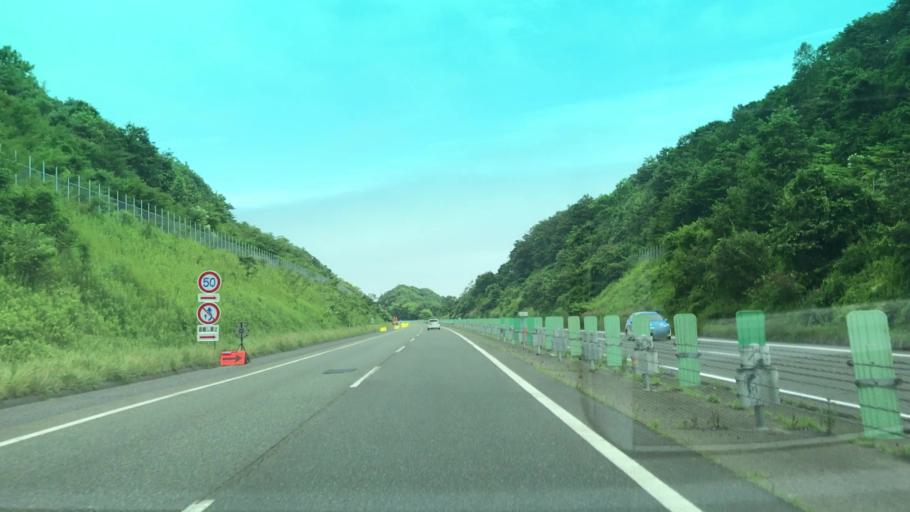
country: JP
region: Hokkaido
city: Shiraoi
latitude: 42.4959
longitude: 141.2508
